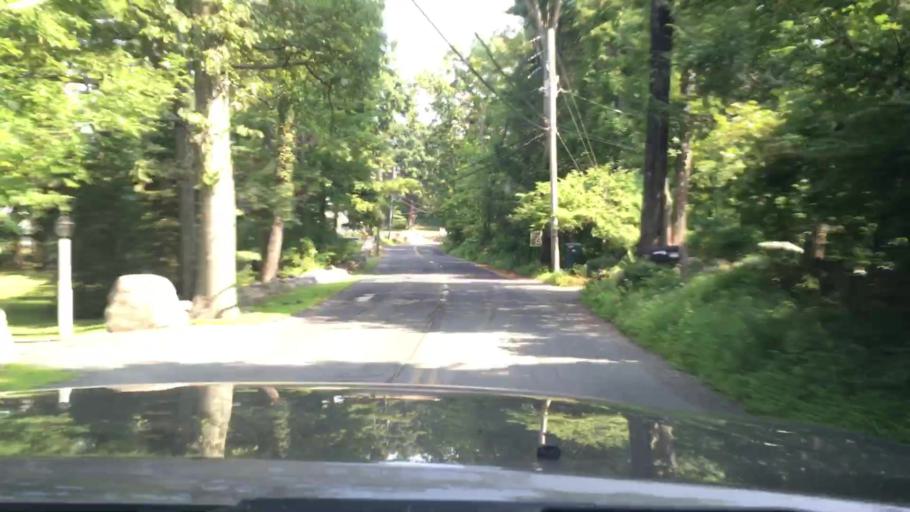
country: US
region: Connecticut
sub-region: Fairfield County
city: Georgetown
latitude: 41.2450
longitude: -73.4555
